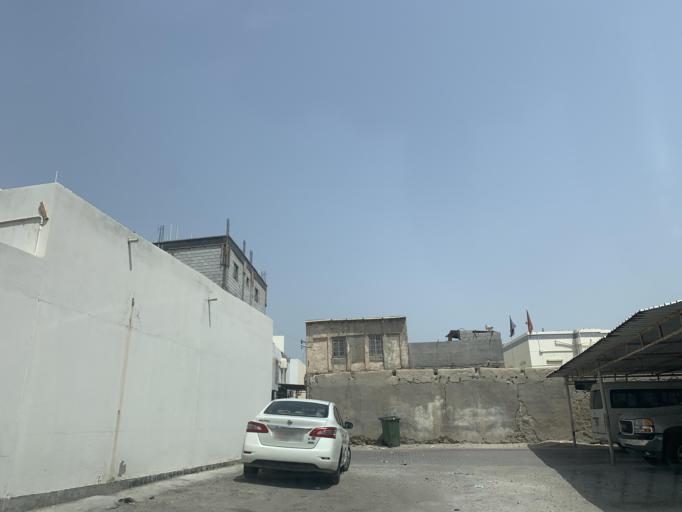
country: BH
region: Northern
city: Madinat `Isa
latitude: 26.1870
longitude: 50.5509
